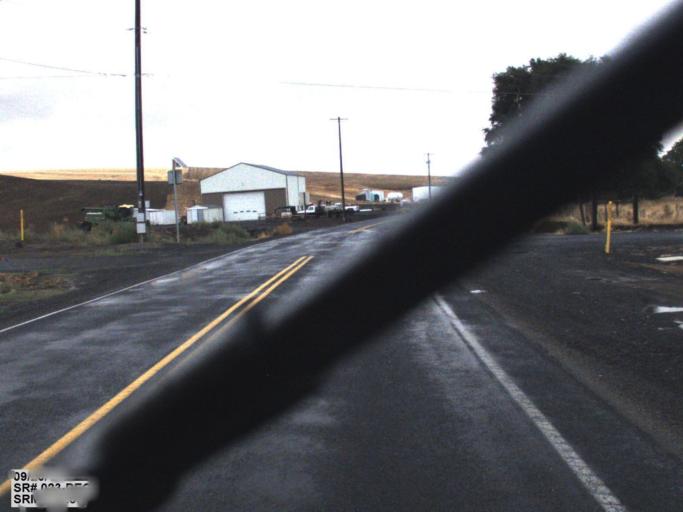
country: US
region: Washington
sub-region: Whitman County
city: Colfax
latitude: 47.0918
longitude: -117.5757
